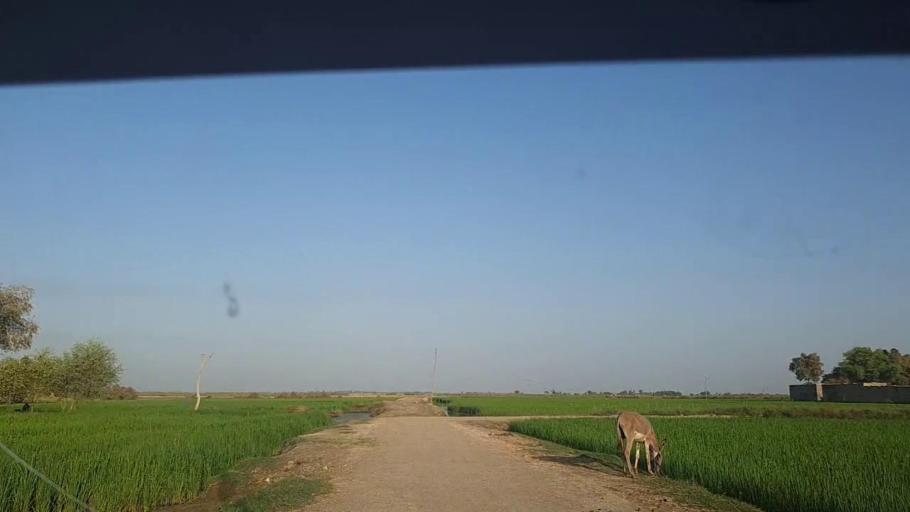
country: PK
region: Sindh
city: Thul
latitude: 28.2116
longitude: 68.8856
